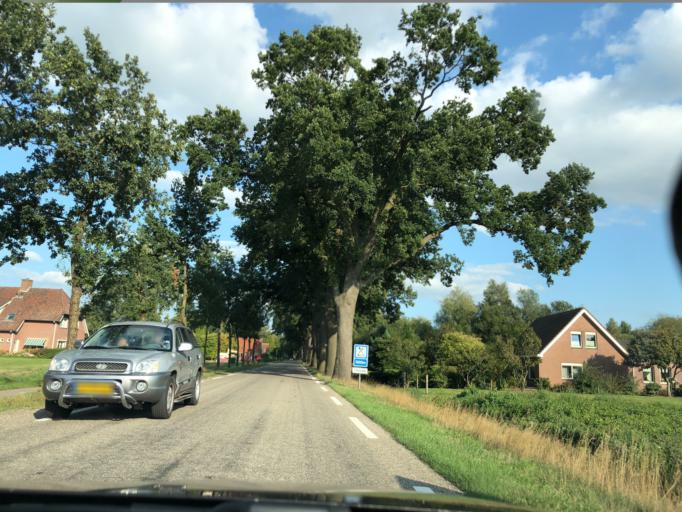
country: NL
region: Groningen
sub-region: Gemeente Vlagtwedde
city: Vlagtwedde
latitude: 53.0240
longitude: 7.1476
